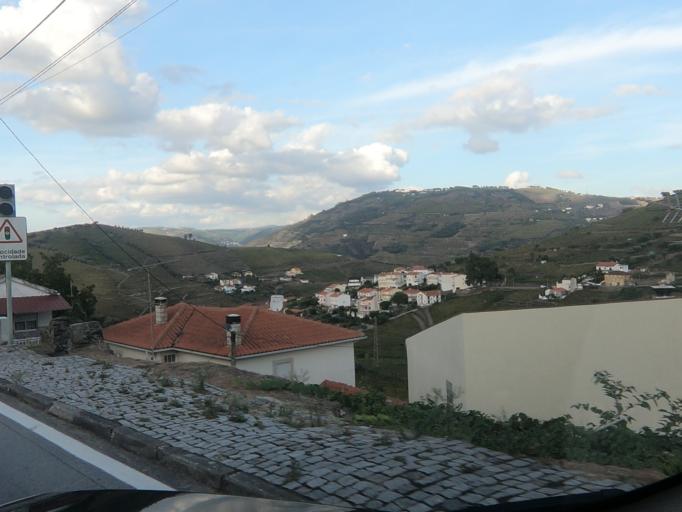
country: PT
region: Vila Real
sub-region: Santa Marta de Penaguiao
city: Santa Marta de Penaguiao
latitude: 41.1928
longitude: -7.7774
